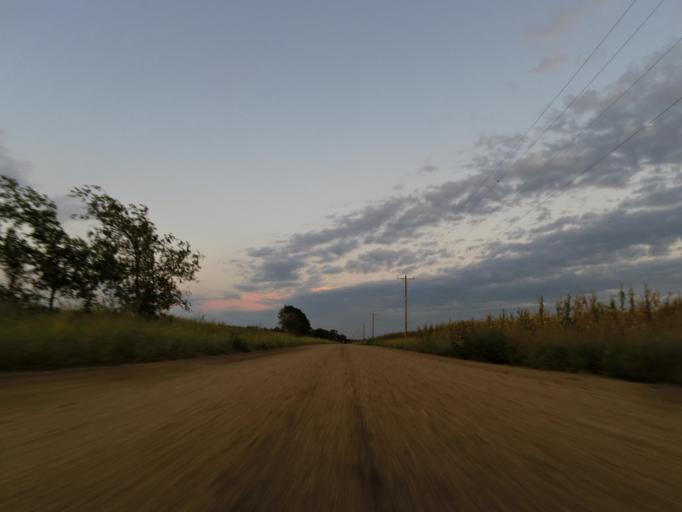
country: US
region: Kansas
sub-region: Reno County
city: South Hutchinson
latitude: 37.9555
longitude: -98.0390
